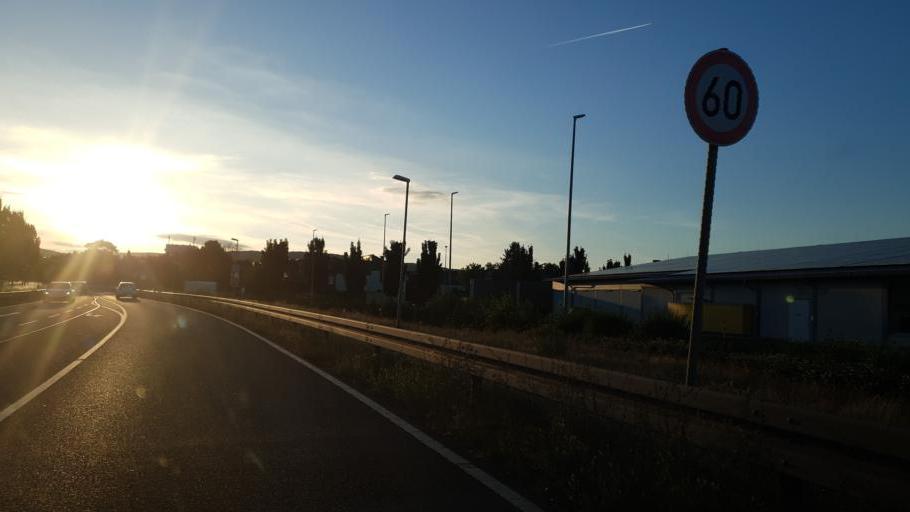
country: DE
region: Hesse
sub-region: Regierungsbezirk Darmstadt
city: Hattersheim
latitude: 50.0775
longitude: 8.4696
